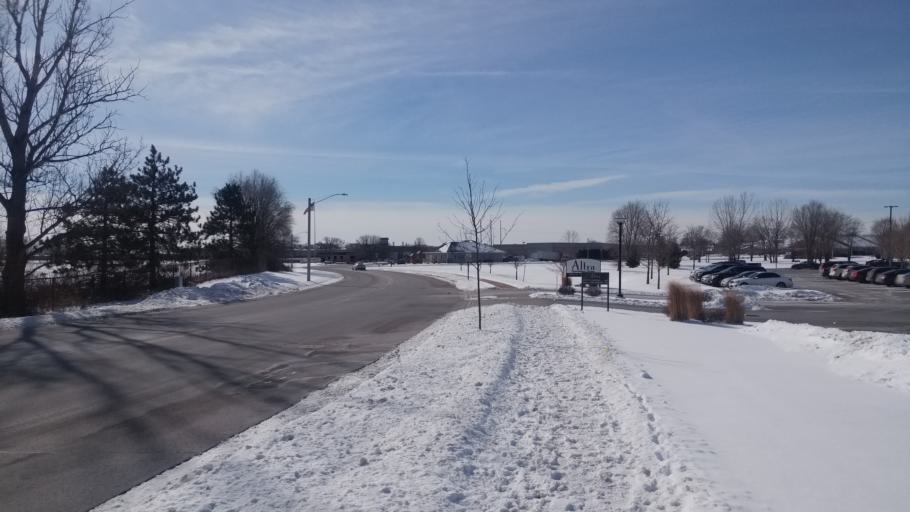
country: US
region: Wisconsin
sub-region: La Crosse County
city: Onalaska
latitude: 43.8760
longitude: -91.2121
